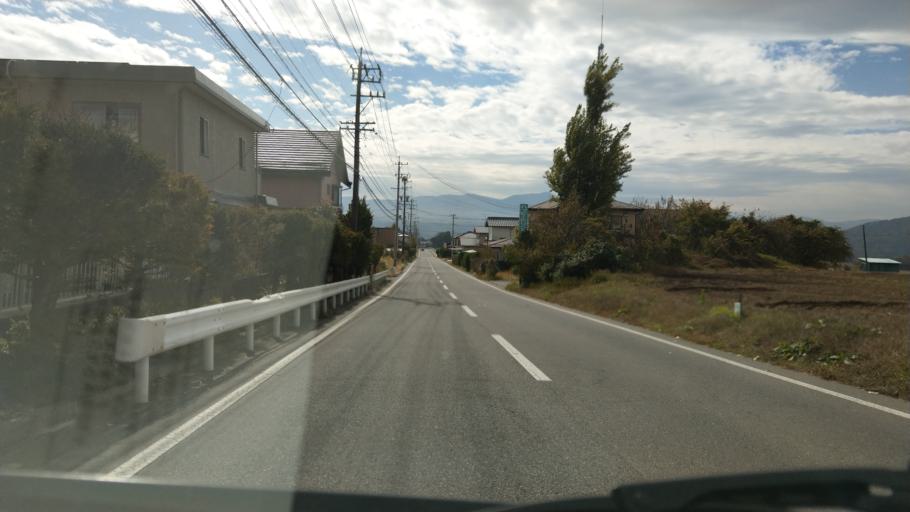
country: JP
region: Nagano
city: Komoro
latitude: 36.3066
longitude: 138.4404
